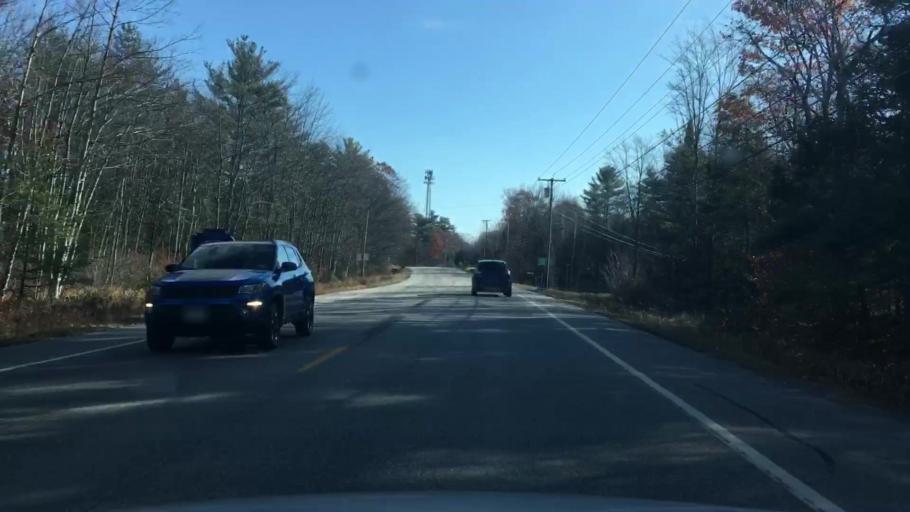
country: US
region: Maine
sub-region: Kennebec County
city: Chelsea
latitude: 44.2810
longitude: -69.6909
